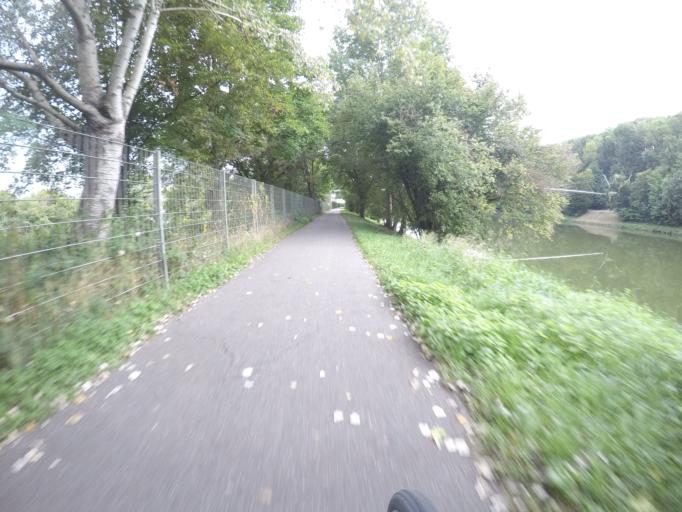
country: DE
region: Baden-Wuerttemberg
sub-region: Regierungsbezirk Stuttgart
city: Stuttgart Muehlhausen
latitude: 48.8526
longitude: 9.2484
